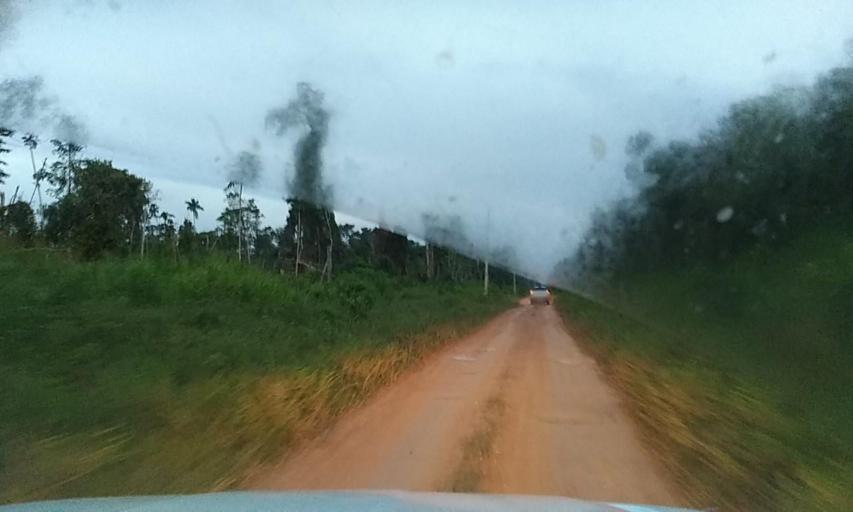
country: BR
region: Para
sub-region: Senador Jose Porfirio
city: Senador Jose Porfirio
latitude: -2.8973
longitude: -51.6862
